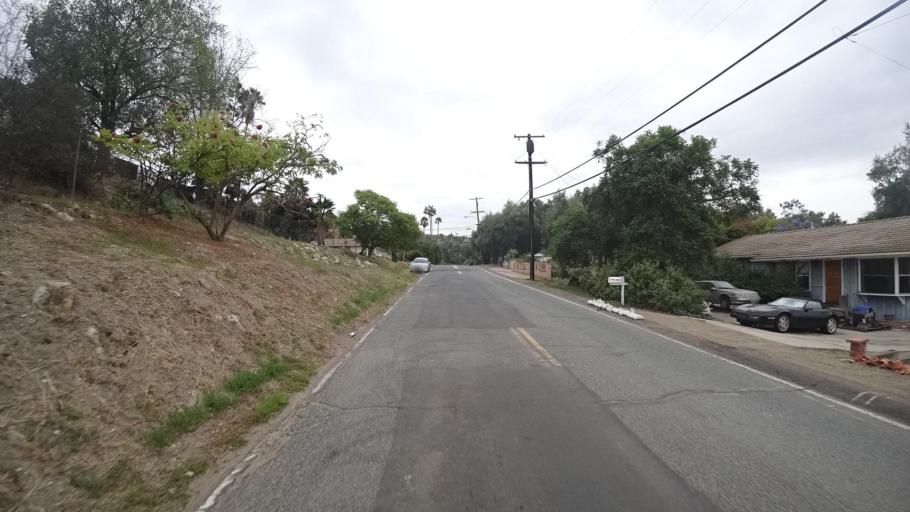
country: US
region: California
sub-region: San Diego County
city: Spring Valley
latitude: 32.7382
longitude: -117.0002
